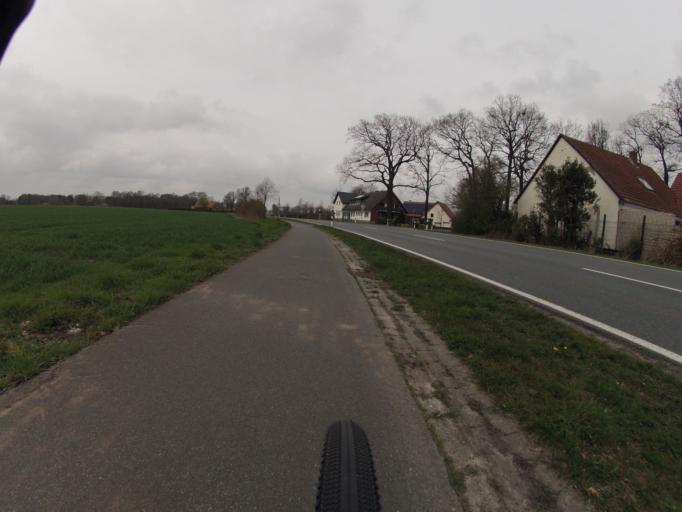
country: DE
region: North Rhine-Westphalia
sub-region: Regierungsbezirk Munster
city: Recke
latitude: 52.3525
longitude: 7.7269
